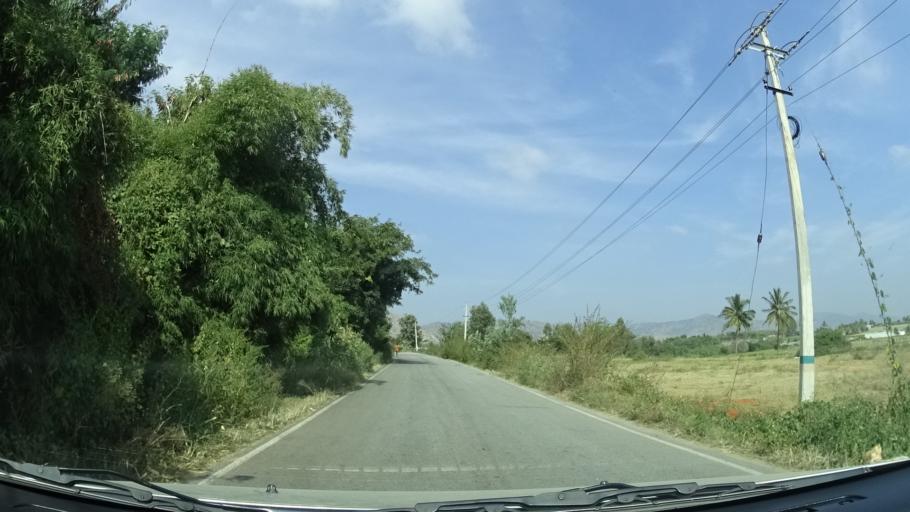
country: IN
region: Karnataka
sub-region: Chikkaballapur
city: Chik Ballapur
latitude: 13.4052
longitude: 77.7182
